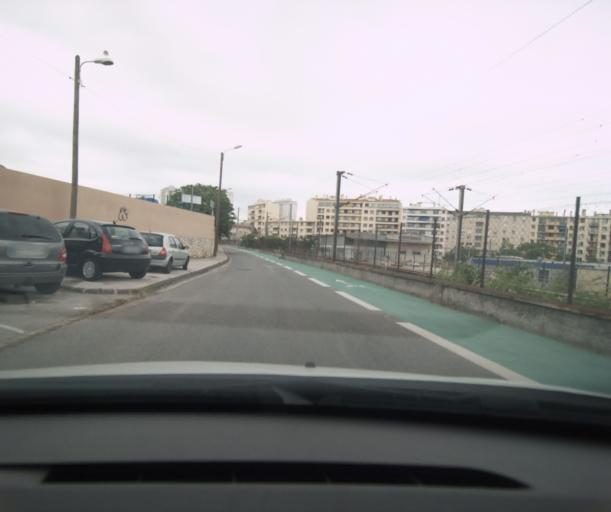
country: FR
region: Provence-Alpes-Cote d'Azur
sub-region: Departement du Var
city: Toulon
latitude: 43.1252
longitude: 5.9392
